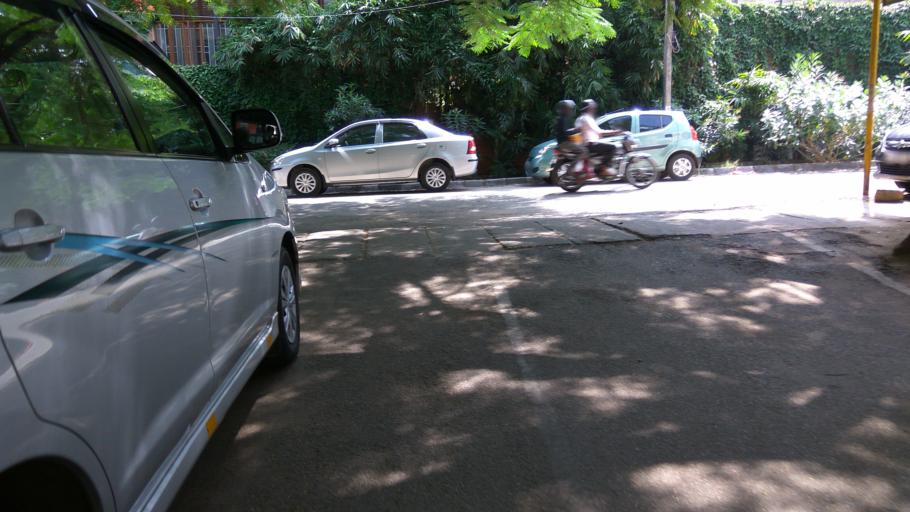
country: IN
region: Karnataka
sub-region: Bangalore Urban
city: Bangalore
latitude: 12.9807
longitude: 77.6399
